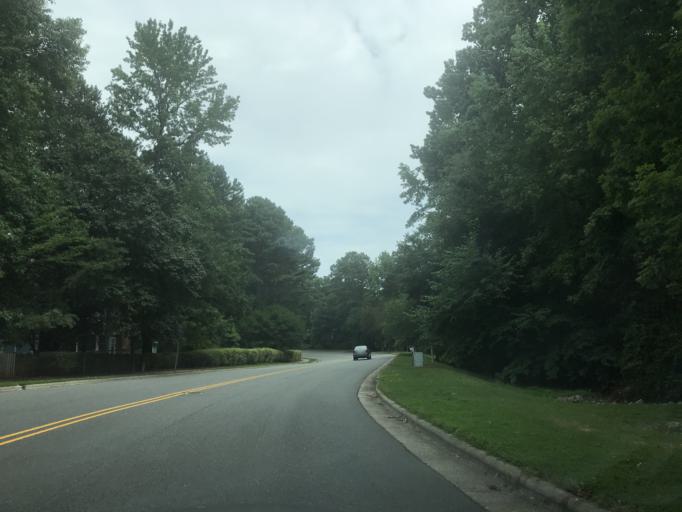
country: US
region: North Carolina
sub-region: Wake County
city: Knightdale
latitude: 35.8066
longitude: -78.5589
